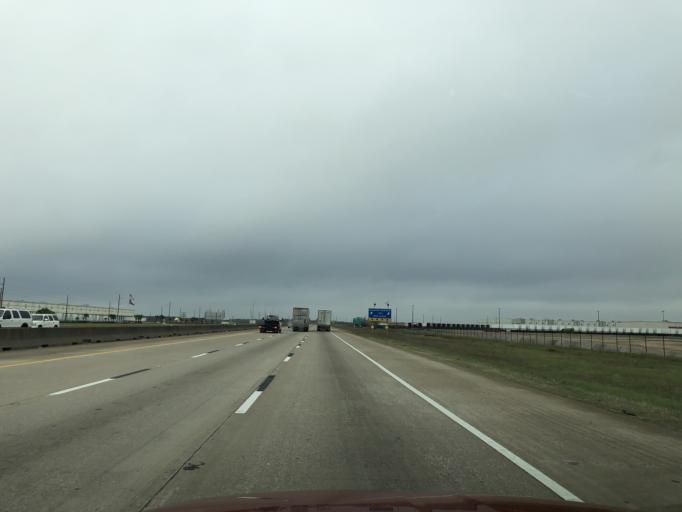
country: US
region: Texas
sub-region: Waller County
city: Brookshire
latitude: 29.7775
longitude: -95.9079
